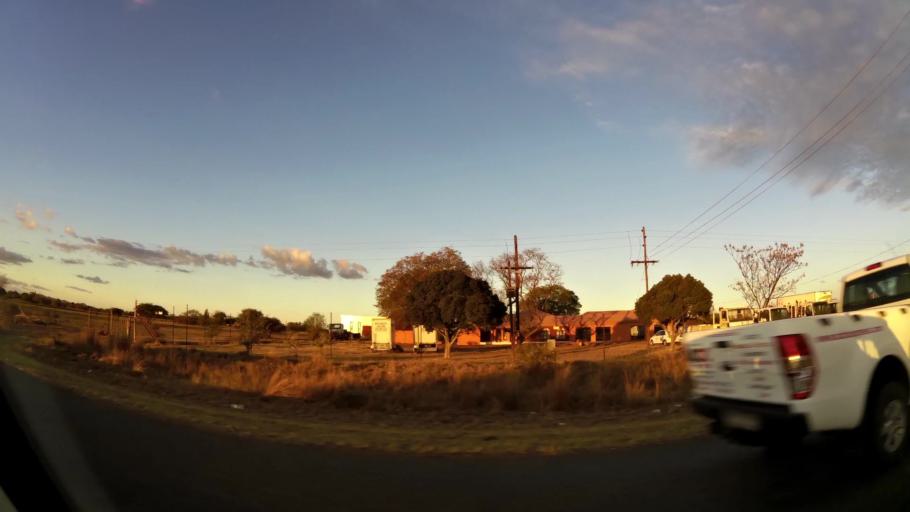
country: ZA
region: Limpopo
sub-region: Capricorn District Municipality
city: Polokwane
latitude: -23.8130
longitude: 29.4802
